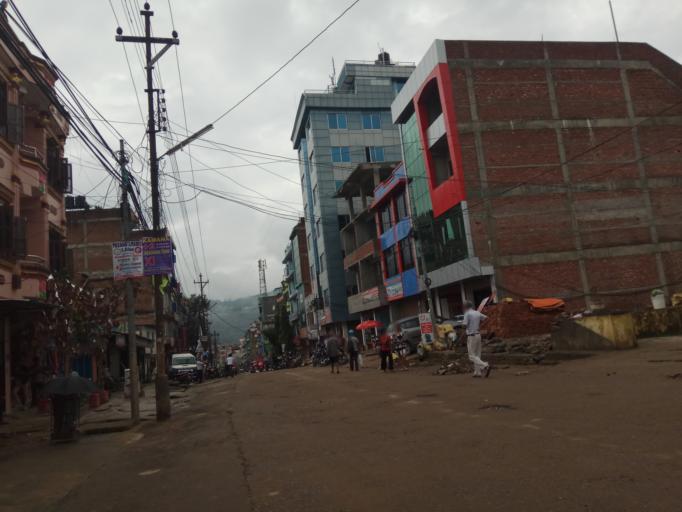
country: NP
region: Central Region
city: Kirtipur
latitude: 27.9111
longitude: 84.8937
